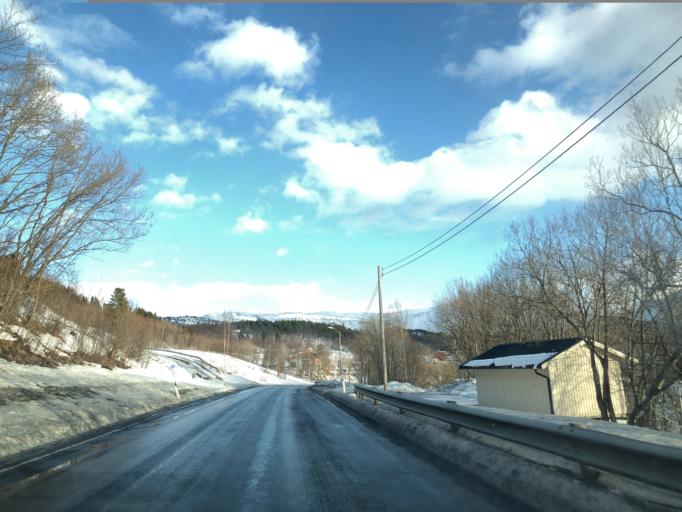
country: NO
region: Nordland
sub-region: Narvik
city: Bjerkvik
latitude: 68.4640
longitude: 17.6816
